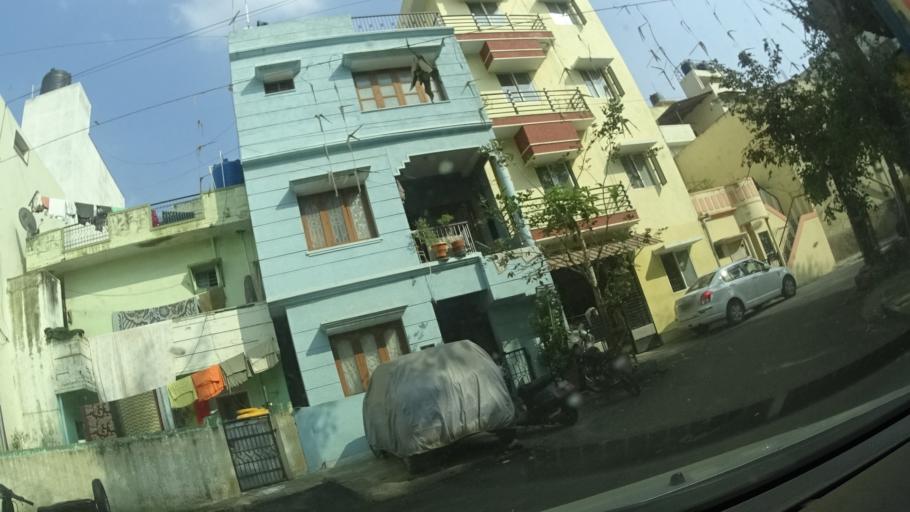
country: IN
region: Karnataka
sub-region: Bangalore Urban
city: Bangalore
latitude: 12.9473
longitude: 77.5598
